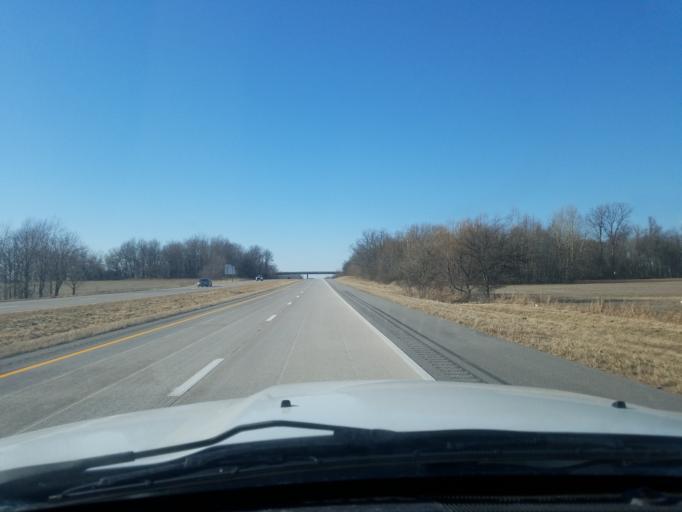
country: US
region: Kentucky
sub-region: Henderson County
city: Henderson
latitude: 37.7925
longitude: -87.4906
